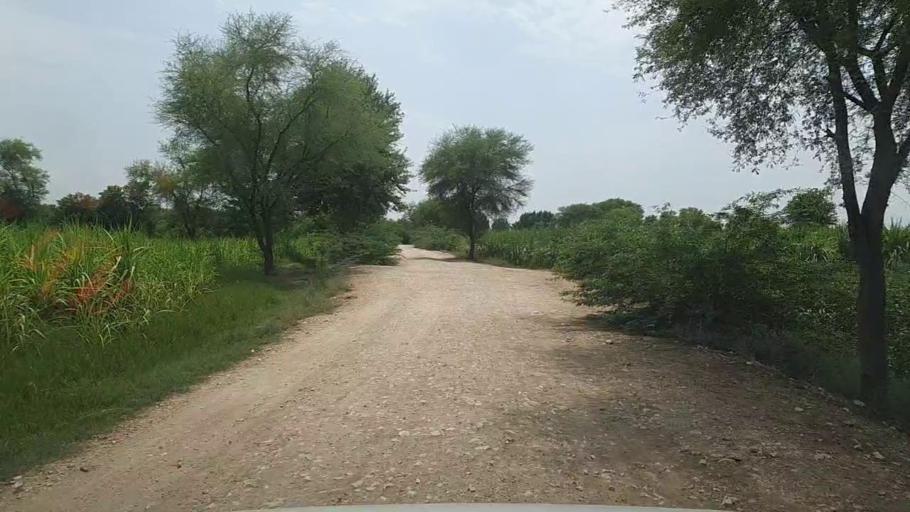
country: PK
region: Sindh
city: Karaundi
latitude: 26.9096
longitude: 68.3219
